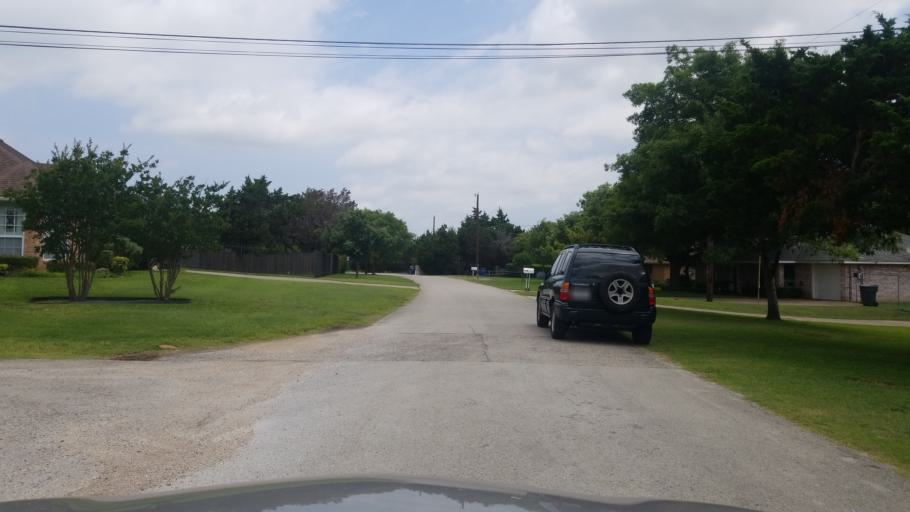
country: US
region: Texas
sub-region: Dallas County
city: Duncanville
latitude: 32.6835
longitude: -96.9310
